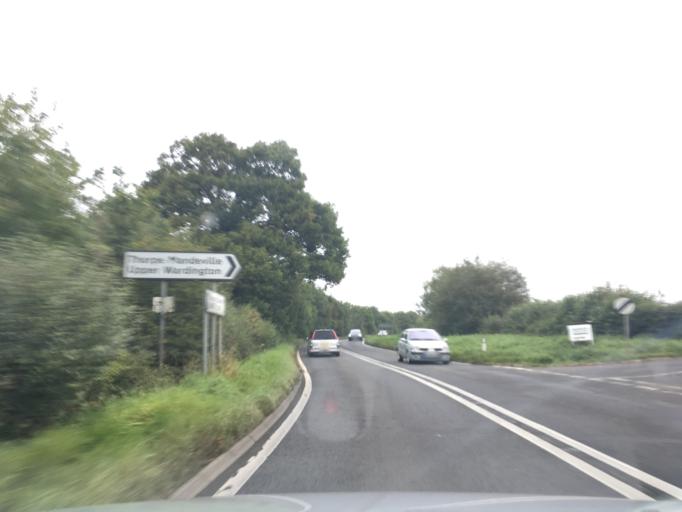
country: GB
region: England
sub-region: Oxfordshire
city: Claydon
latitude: 52.1065
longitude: -1.2935
